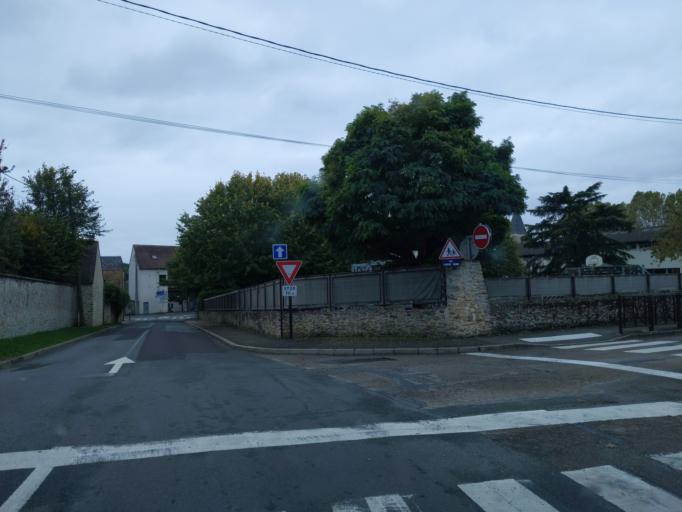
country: FR
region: Ile-de-France
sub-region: Departement des Yvelines
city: Saint-Arnoult-en-Yvelines
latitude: 48.5737
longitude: 1.9421
